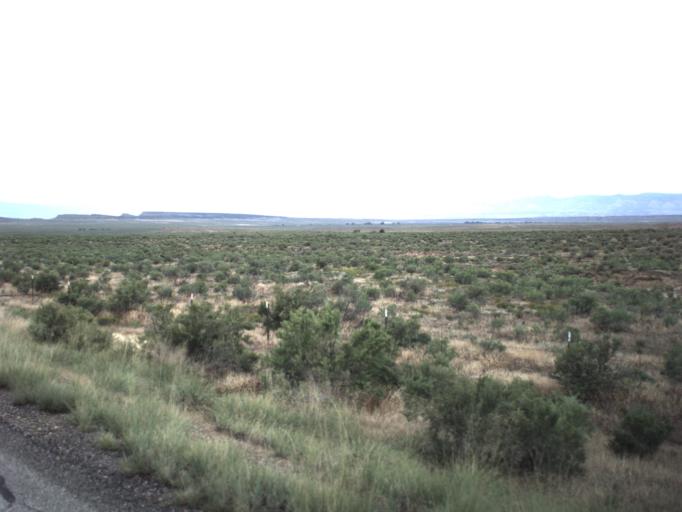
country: US
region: Utah
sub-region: Carbon County
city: East Carbon City
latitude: 39.5329
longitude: -110.5355
